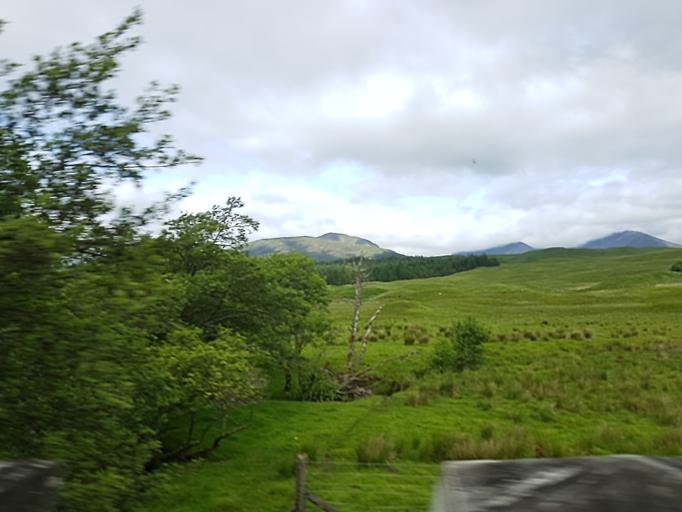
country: GB
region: Scotland
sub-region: Highland
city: Spean Bridge
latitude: 56.5613
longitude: -4.7460
